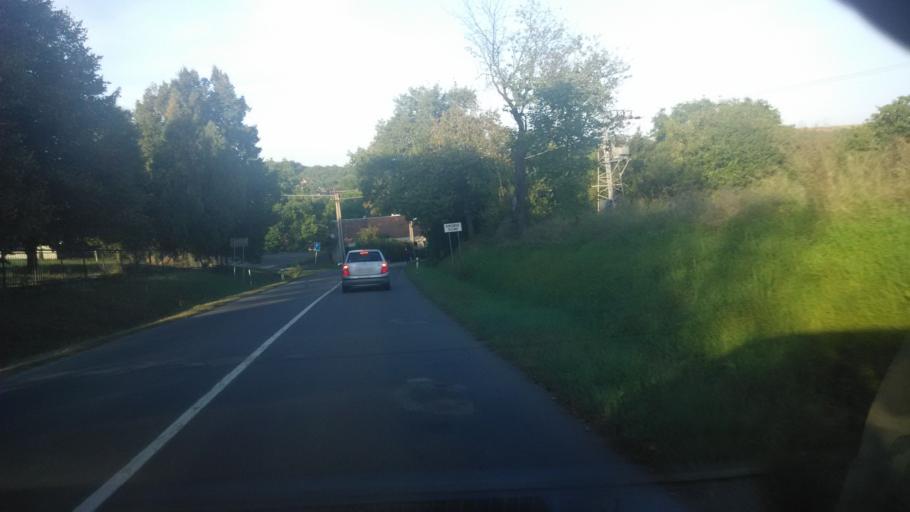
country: SK
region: Banskobystricky
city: Dudince
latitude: 48.2065
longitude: 18.7997
